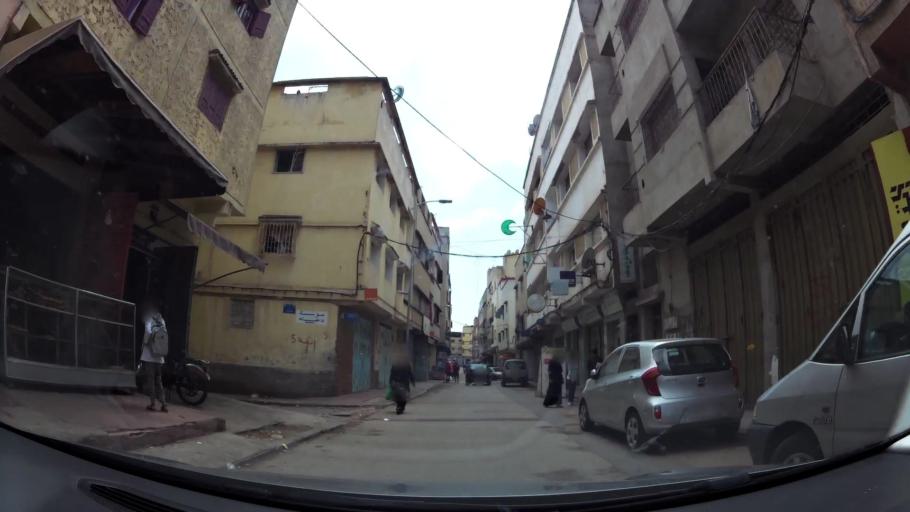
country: MA
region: Rabat-Sale-Zemmour-Zaer
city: Sale
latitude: 34.0504
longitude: -6.8186
